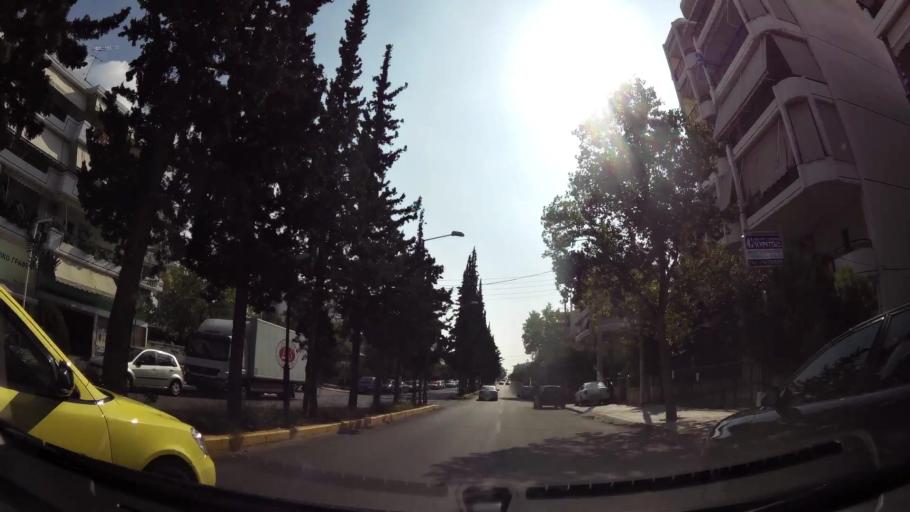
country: GR
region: Attica
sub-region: Nomarchia Athinas
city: Ilioupoli
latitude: 37.9265
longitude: 23.7511
